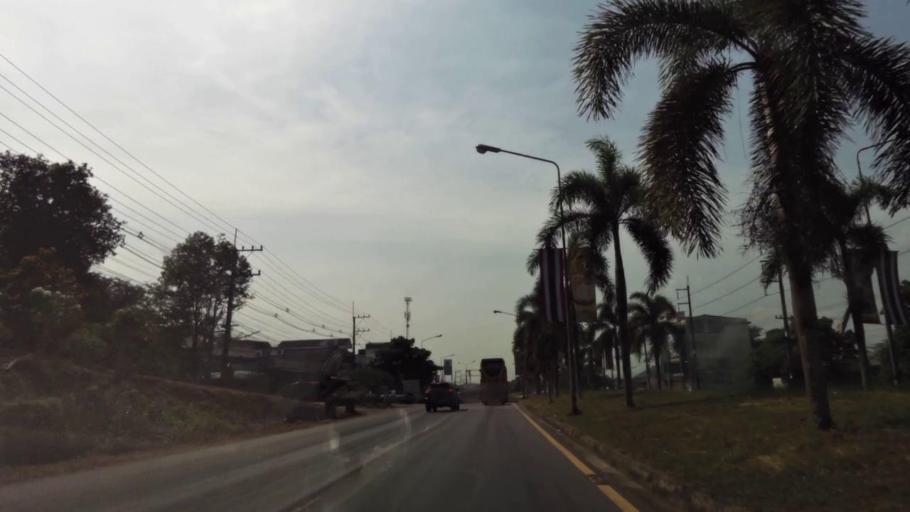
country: TH
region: Chanthaburi
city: Chanthaburi
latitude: 12.6665
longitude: 102.0934
